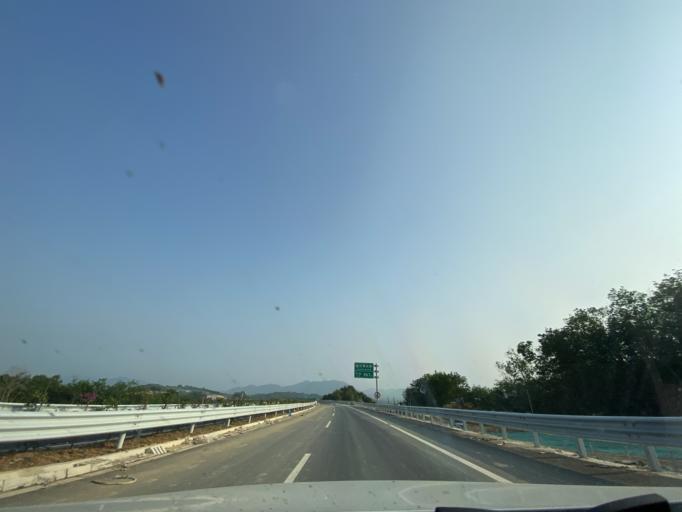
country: CN
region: Hainan
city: Xiangshui
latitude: 18.6400
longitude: 109.6293
